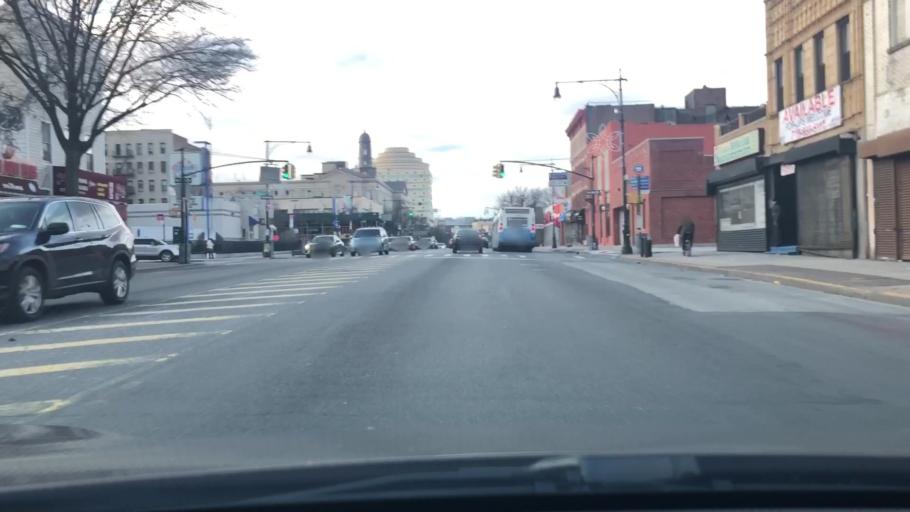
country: US
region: New York
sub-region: Bronx
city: The Bronx
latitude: 40.8587
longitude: -73.8855
